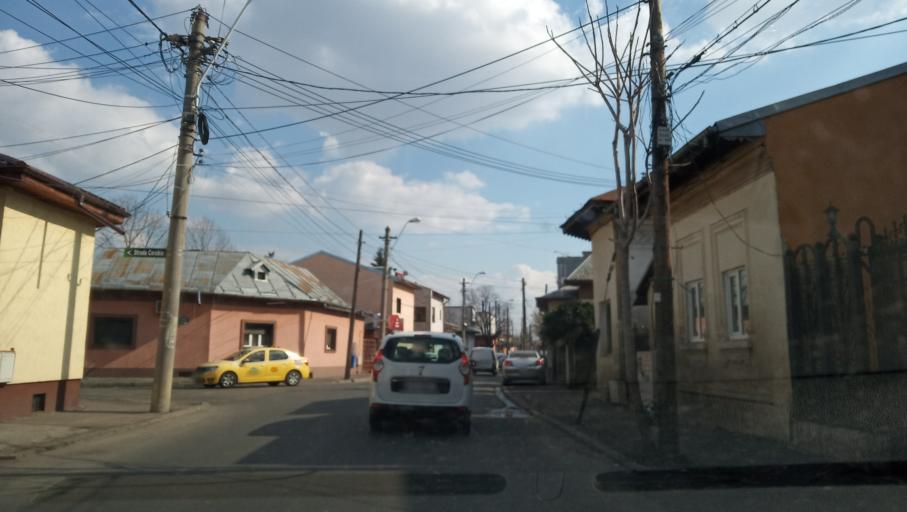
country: RO
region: Ilfov
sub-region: Comuna Fundeni-Dobroesti
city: Fundeni
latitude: 44.4557
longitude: 26.1328
